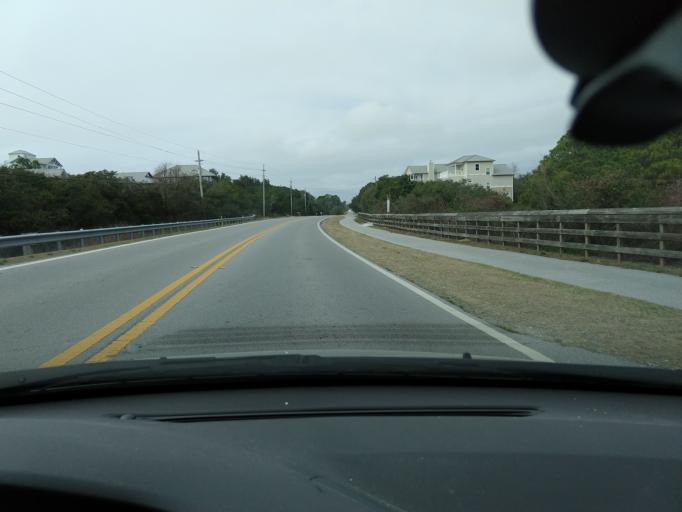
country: US
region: Florida
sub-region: Walton County
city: Miramar Beach
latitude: 30.3553
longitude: -86.2577
